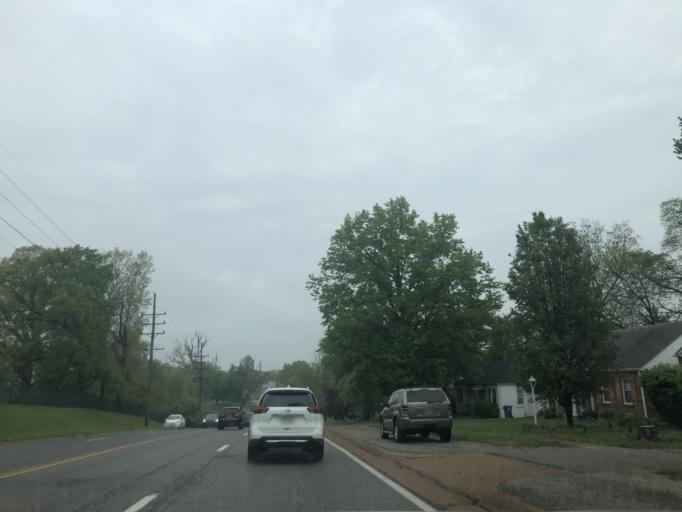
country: US
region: Missouri
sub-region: Saint Louis County
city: Marlborough
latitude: 38.5787
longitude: -90.3186
